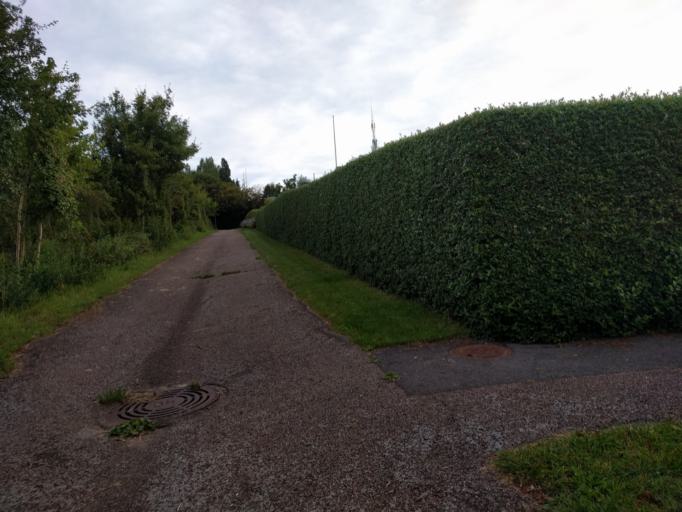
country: DK
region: South Denmark
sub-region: Kerteminde Kommune
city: Munkebo
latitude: 55.4662
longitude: 10.5744
